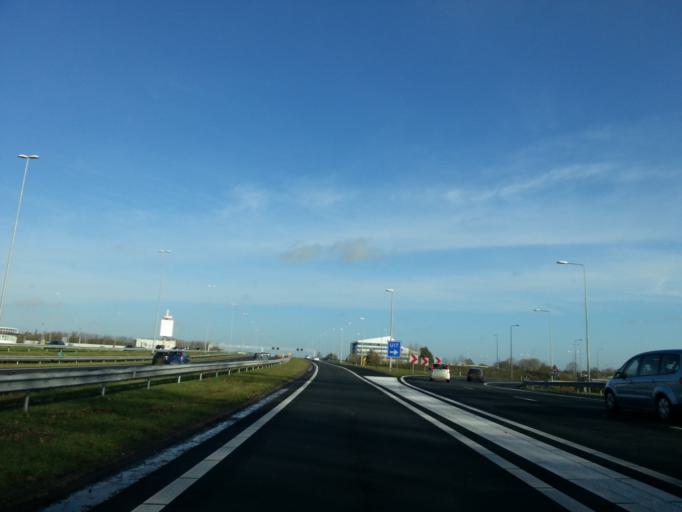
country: NL
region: South Holland
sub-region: Gemeente Leiden
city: Leiden
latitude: 52.1375
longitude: 4.5068
